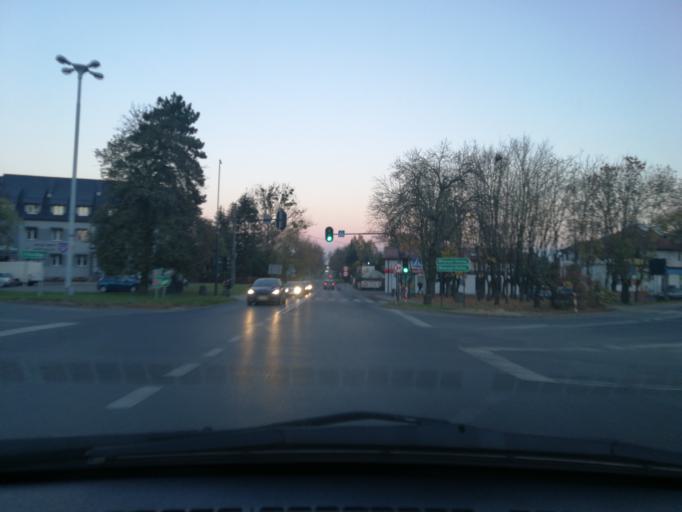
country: PL
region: Lodz Voivodeship
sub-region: Powiat lodzki wschodni
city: Andrespol
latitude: 51.7938
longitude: 19.5896
